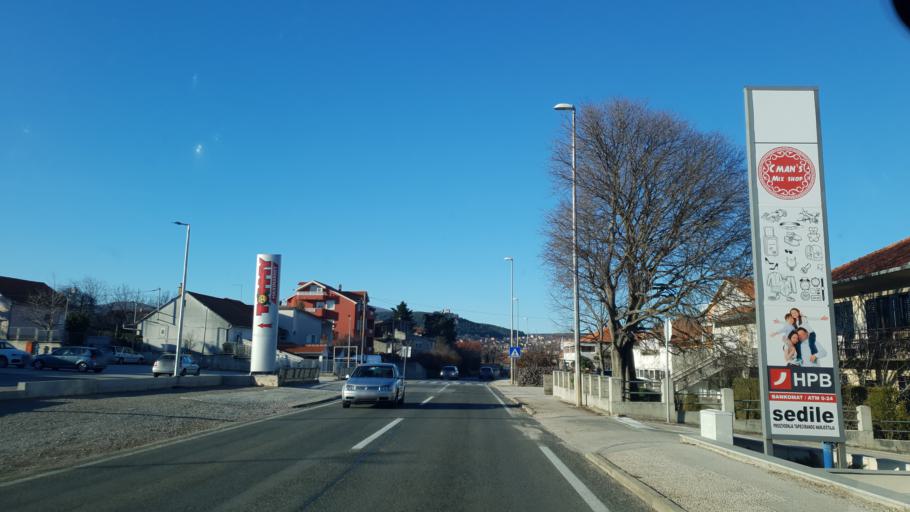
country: HR
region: Splitsko-Dalmatinska
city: Brnaze
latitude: 43.6901
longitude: 16.6467
